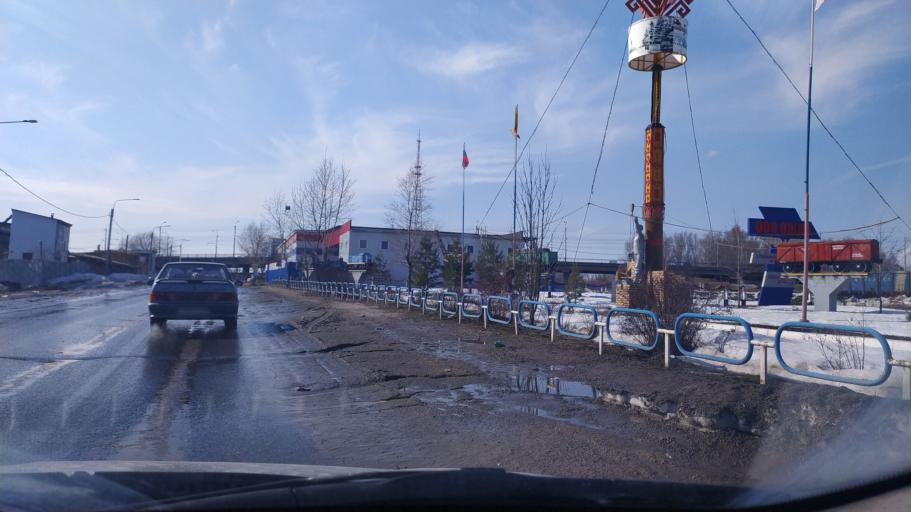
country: RU
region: Chuvashia
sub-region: Cheboksarskiy Rayon
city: Cheboksary
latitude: 56.1178
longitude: 47.2794
